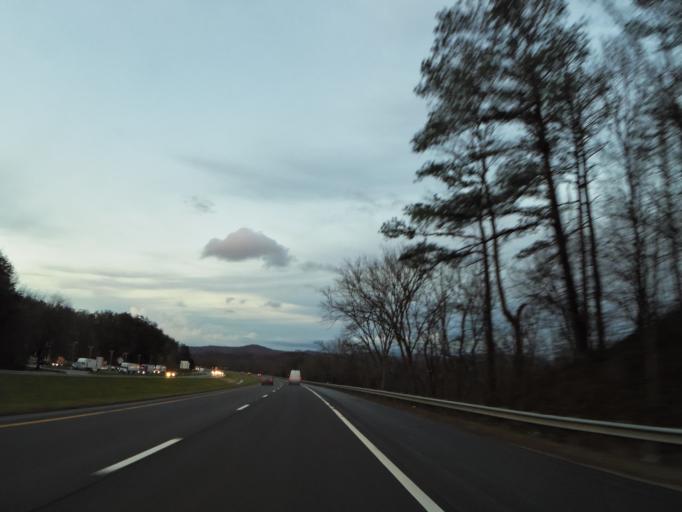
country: US
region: Tennessee
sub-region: Campbell County
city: Jellico
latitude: 36.5863
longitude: -84.1055
